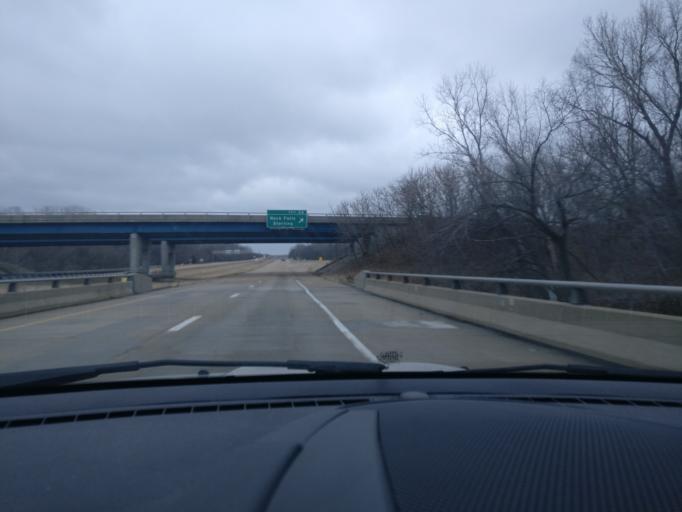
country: US
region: Illinois
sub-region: Whiteside County
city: Sterling
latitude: 41.7598
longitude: -89.7847
